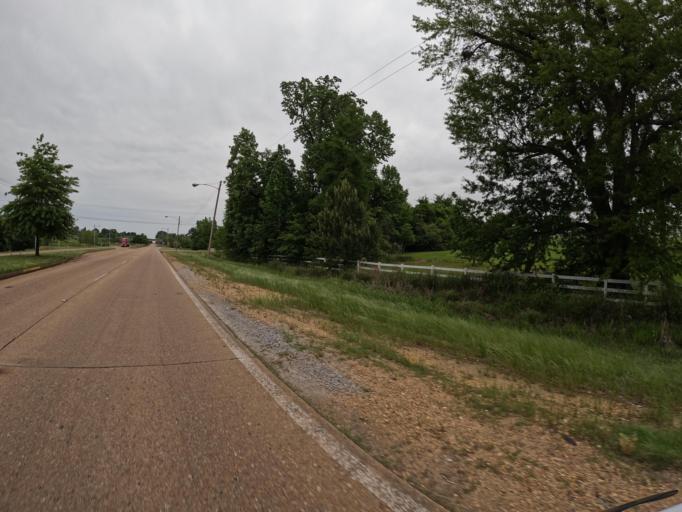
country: US
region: Mississippi
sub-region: Lee County
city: Tupelo
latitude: 34.2766
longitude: -88.7219
